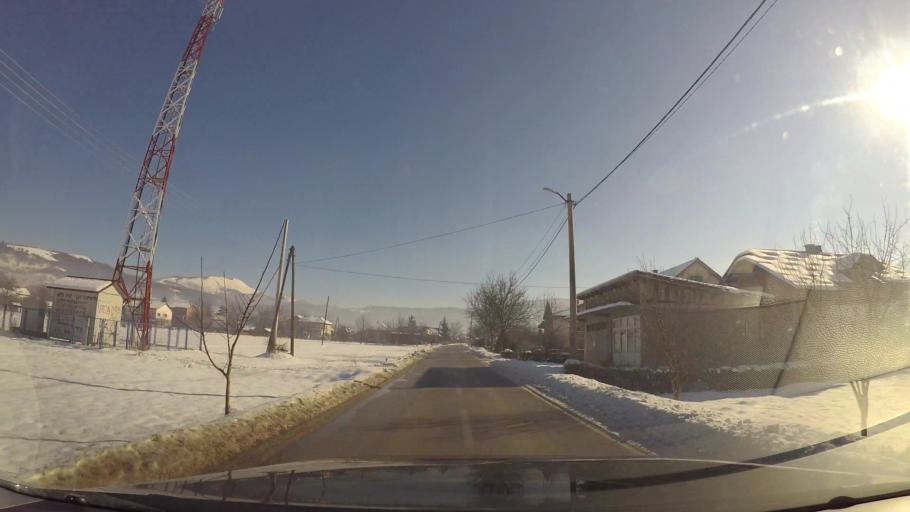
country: BA
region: Federation of Bosnia and Herzegovina
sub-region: Kanton Sarajevo
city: Sarajevo
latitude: 43.7964
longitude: 18.3453
